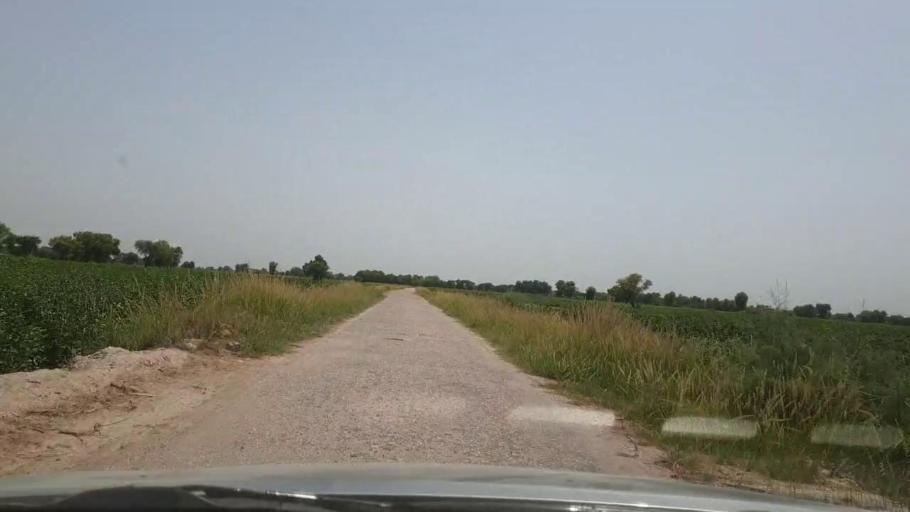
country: PK
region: Sindh
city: Pano Aqil
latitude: 27.8020
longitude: 69.2419
